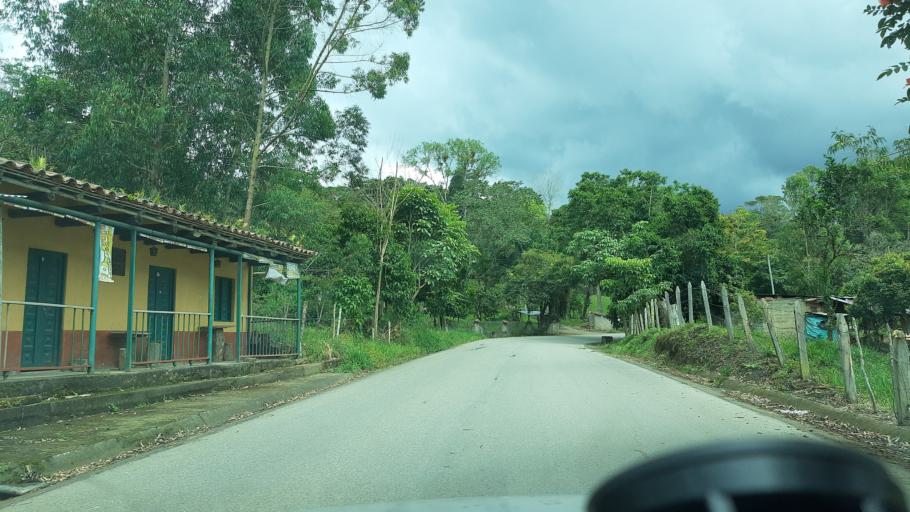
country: CO
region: Boyaca
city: Garagoa
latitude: 5.1010
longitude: -73.3698
